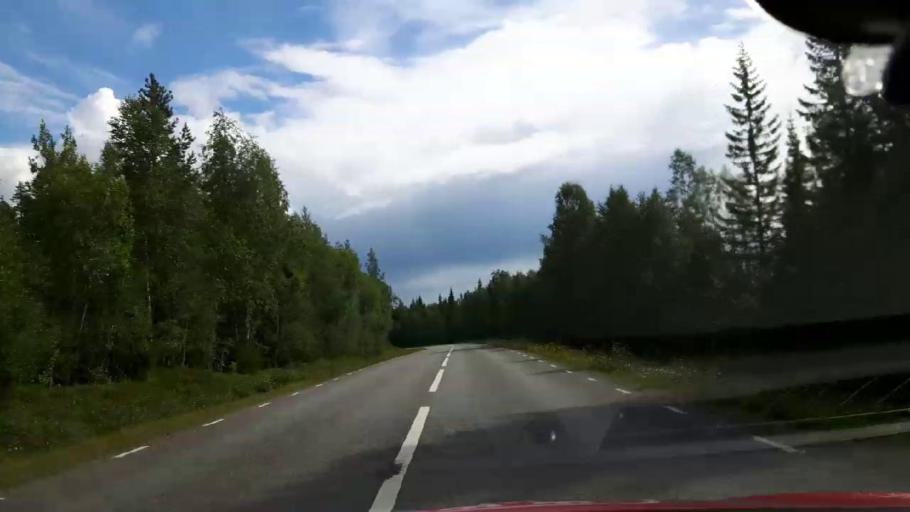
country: SE
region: Jaemtland
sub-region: Stroemsunds Kommun
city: Stroemsund
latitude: 64.3433
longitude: 15.1081
